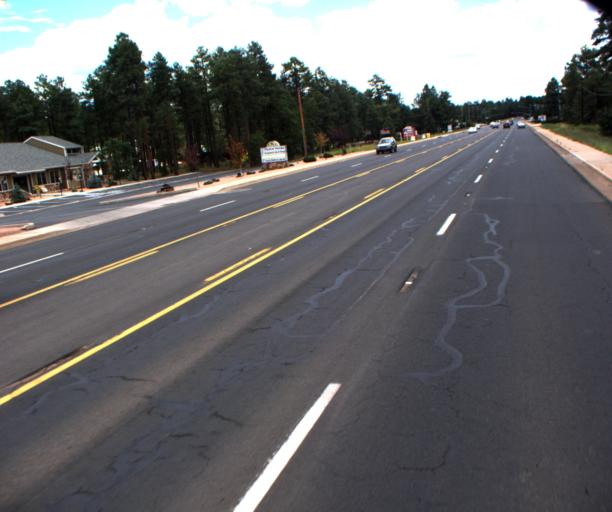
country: US
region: Arizona
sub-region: Navajo County
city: Pinetop-Lakeside
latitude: 34.1450
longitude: -109.9581
